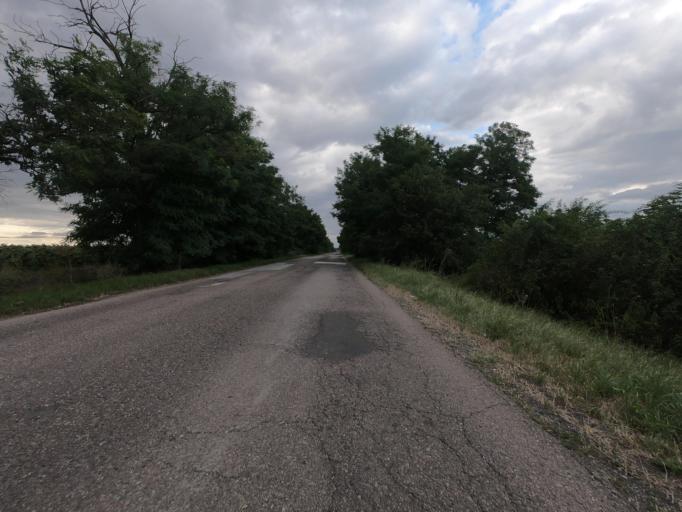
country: HU
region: Heves
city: Poroszlo
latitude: 47.6833
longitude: 20.6520
